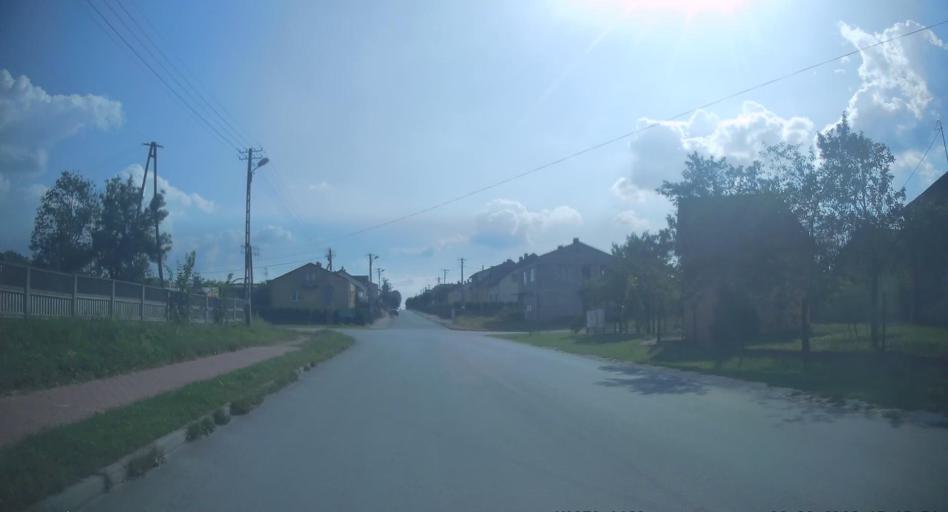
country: PL
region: Swietokrzyskie
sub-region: Powiat konecki
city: Radoszyce
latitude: 51.0786
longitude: 20.2560
